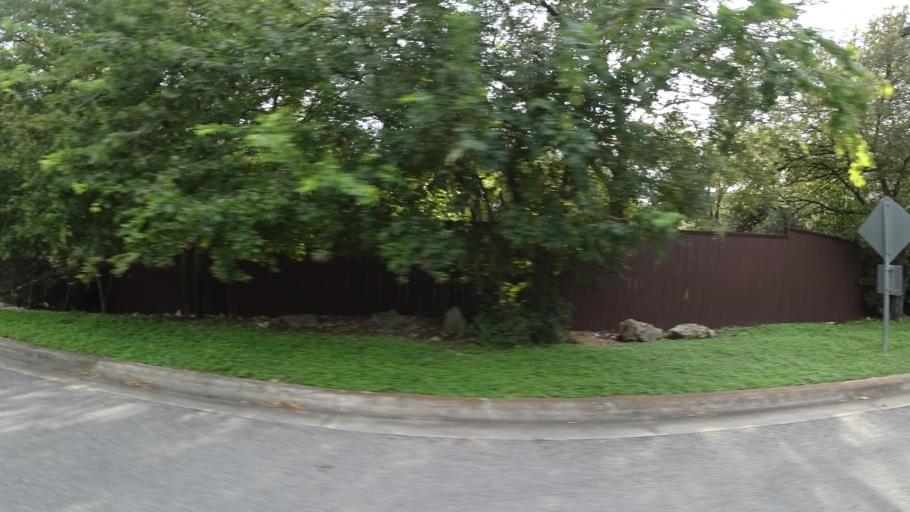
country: US
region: Texas
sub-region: Travis County
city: Rollingwood
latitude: 30.2780
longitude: -97.7851
